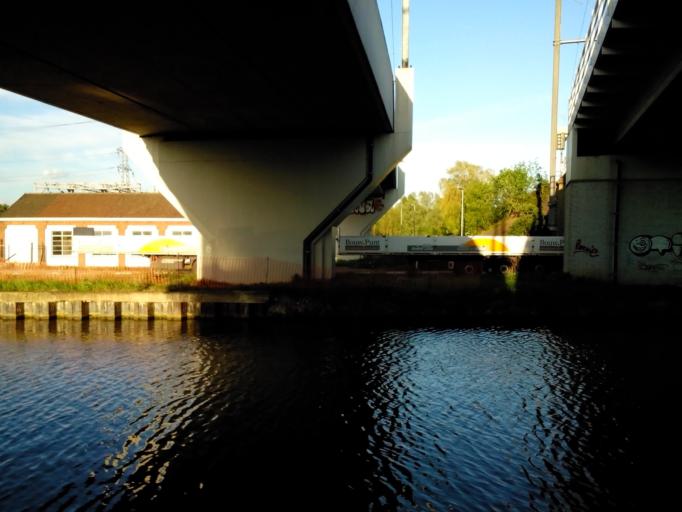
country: BE
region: Flanders
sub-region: Provincie Vlaams-Brabant
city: Leuven
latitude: 50.9014
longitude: 4.7065
